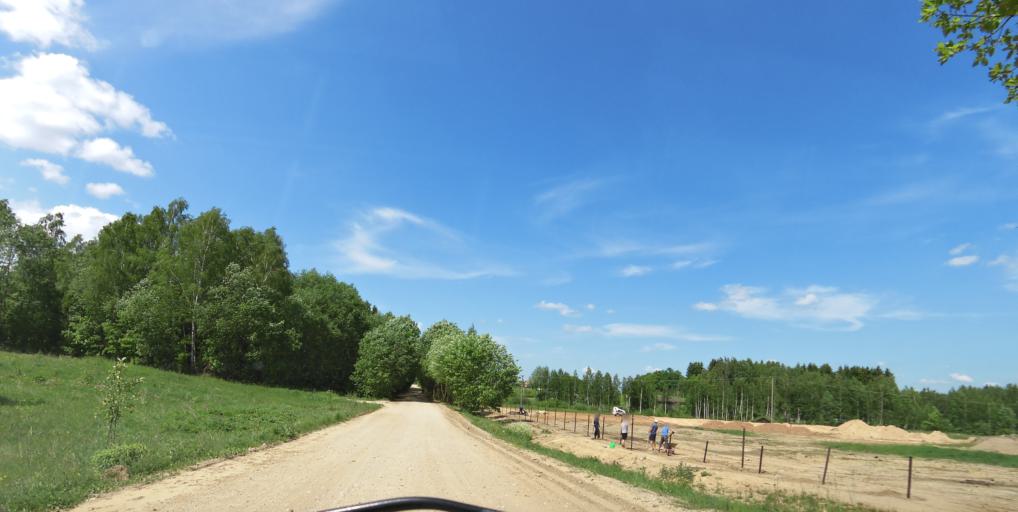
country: LT
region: Vilnius County
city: Pilaite
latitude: 54.7429
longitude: 25.1381
